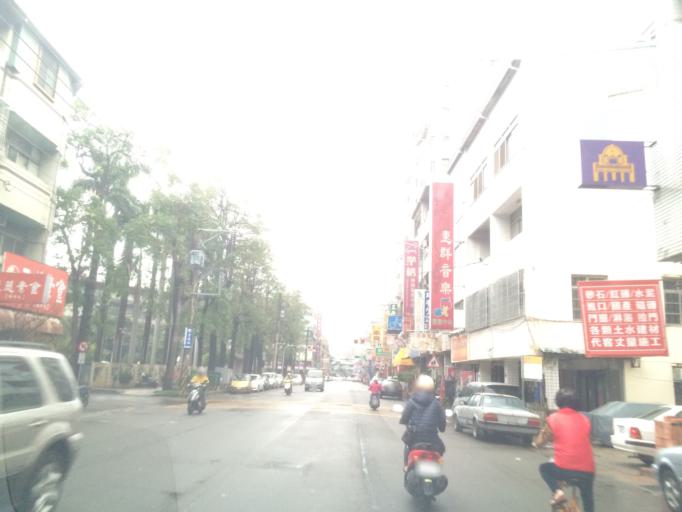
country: TW
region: Taiwan
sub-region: Taichung City
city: Taichung
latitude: 24.1814
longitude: 120.6889
